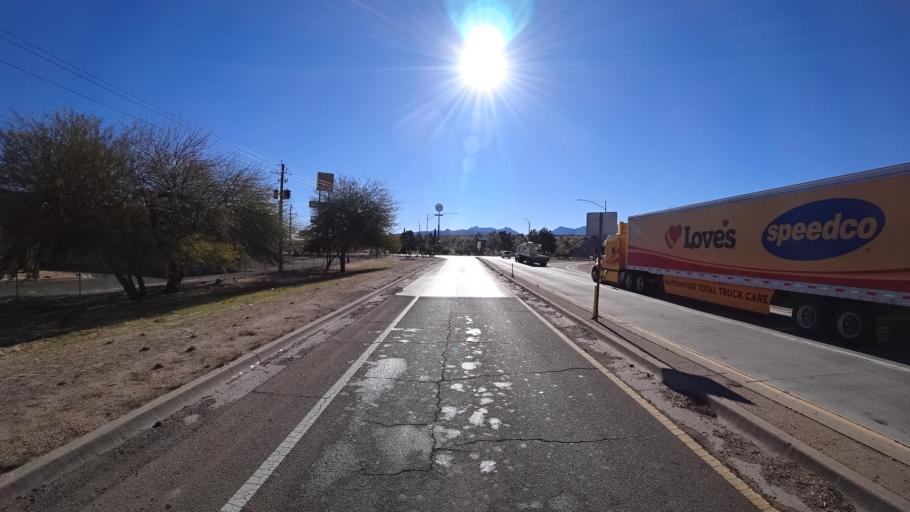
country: US
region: Arizona
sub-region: Mohave County
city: New Kingman-Butler
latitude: 35.2186
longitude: -114.0109
